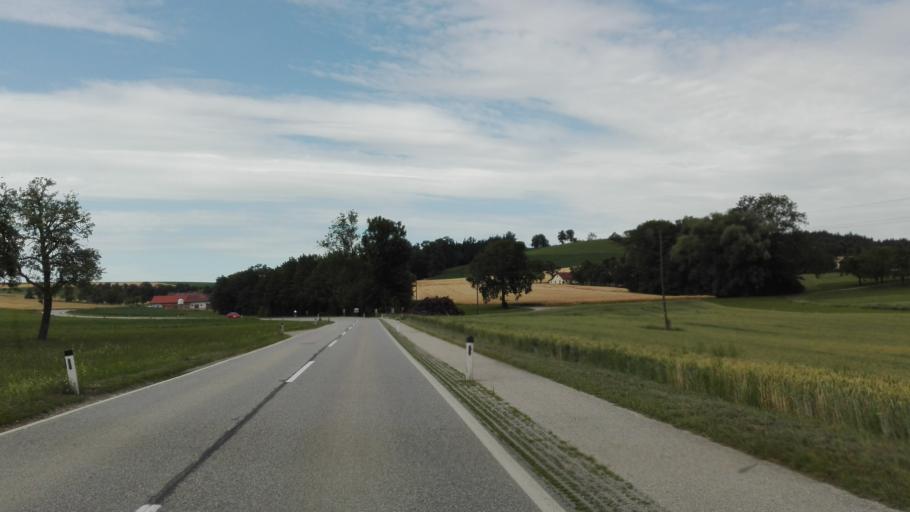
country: AT
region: Upper Austria
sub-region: Politischer Bezirk Grieskirchen
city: Grieskirchen
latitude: 48.2494
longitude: 13.8129
